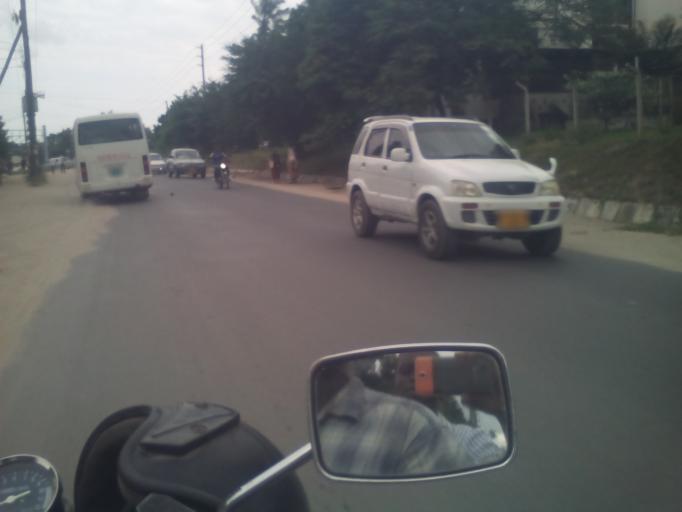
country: TZ
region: Dar es Salaam
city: Dar es Salaam
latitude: -6.8451
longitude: 39.2734
